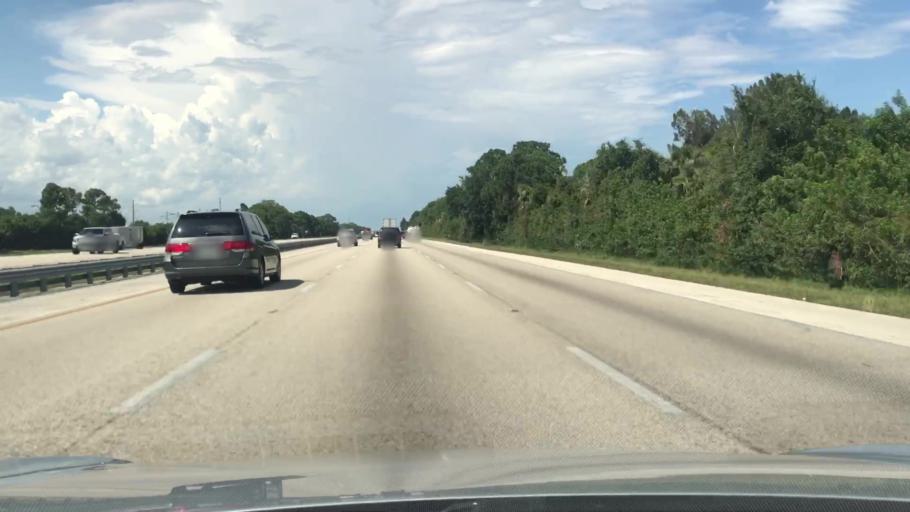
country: US
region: Florida
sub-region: Brevard County
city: June Park
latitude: 28.1611
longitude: -80.7056
